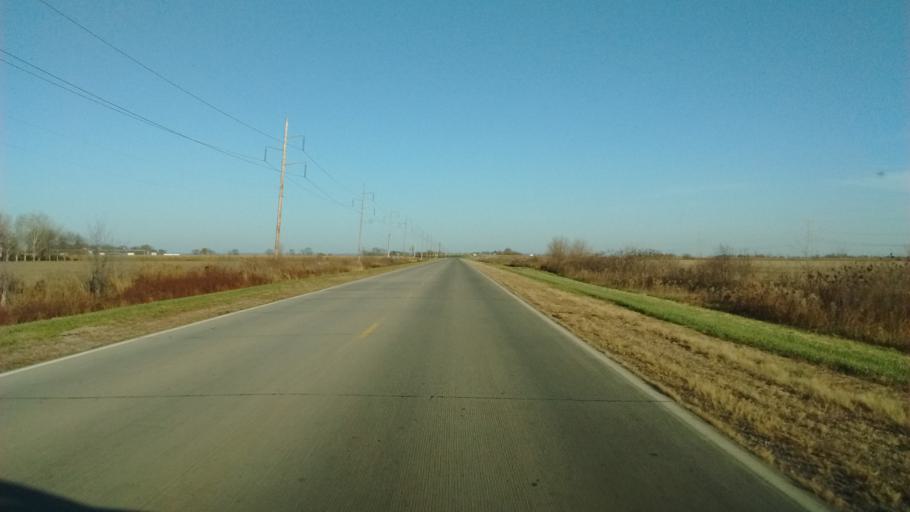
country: US
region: Iowa
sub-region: Woodbury County
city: Sergeant Bluff
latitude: 42.3302
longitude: -96.3341
